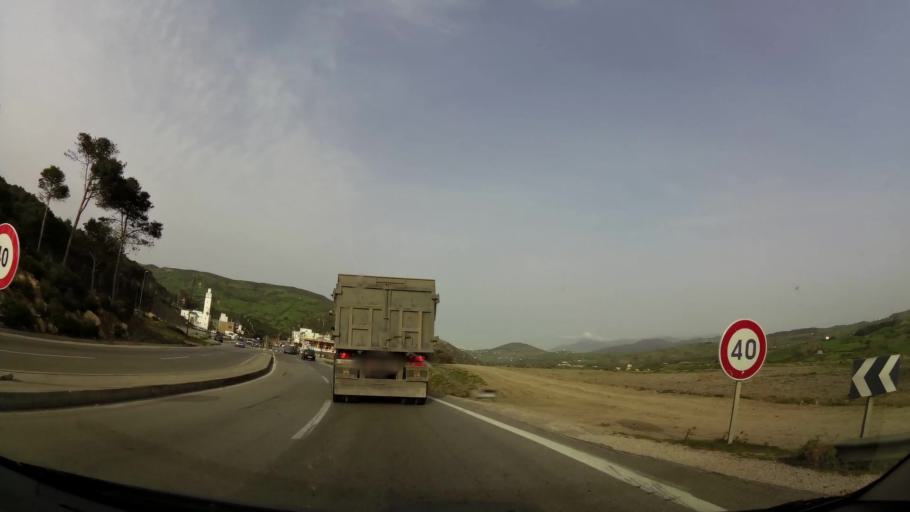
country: MA
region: Tanger-Tetouan
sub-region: Tetouan
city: Saddina
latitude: 35.5460
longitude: -5.5581
